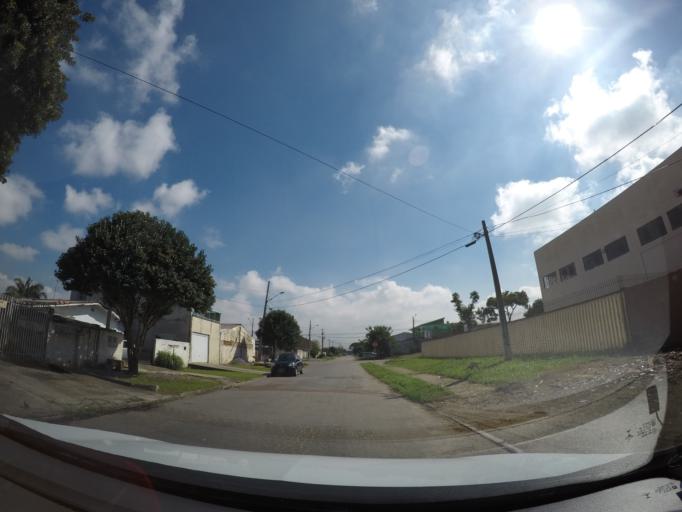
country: BR
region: Parana
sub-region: Sao Jose Dos Pinhais
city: Sao Jose dos Pinhais
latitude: -25.5033
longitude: -49.2163
